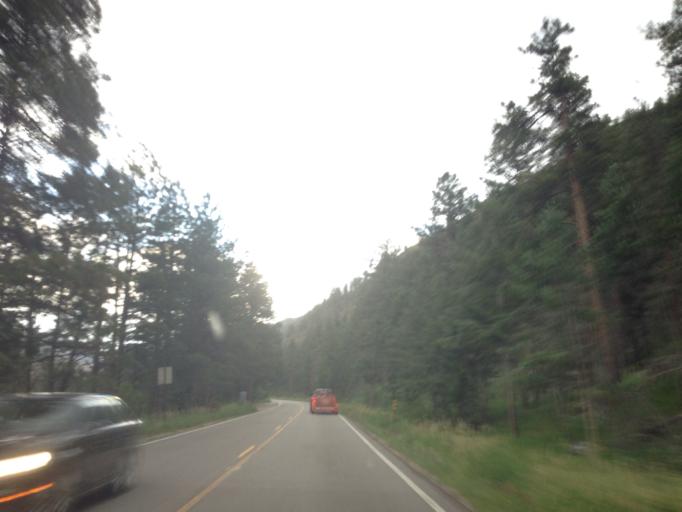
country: US
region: Colorado
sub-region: Larimer County
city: Laporte
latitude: 40.6877
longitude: -105.3566
